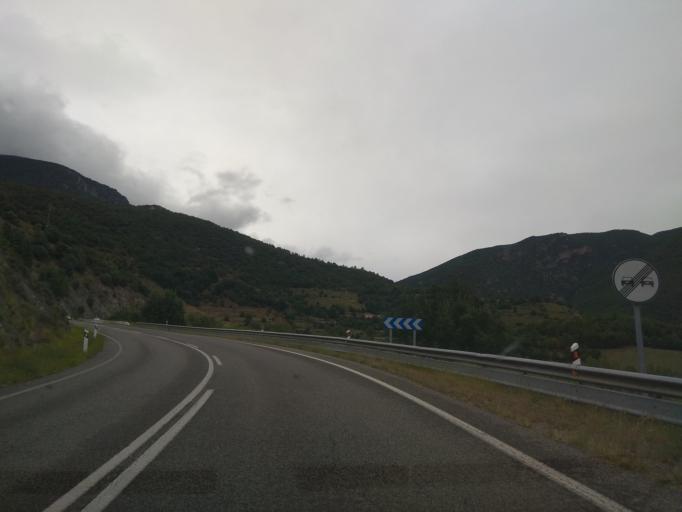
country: ES
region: Catalonia
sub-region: Provincia de Lleida
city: el Pont de Bar
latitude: 42.3597
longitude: 1.5691
